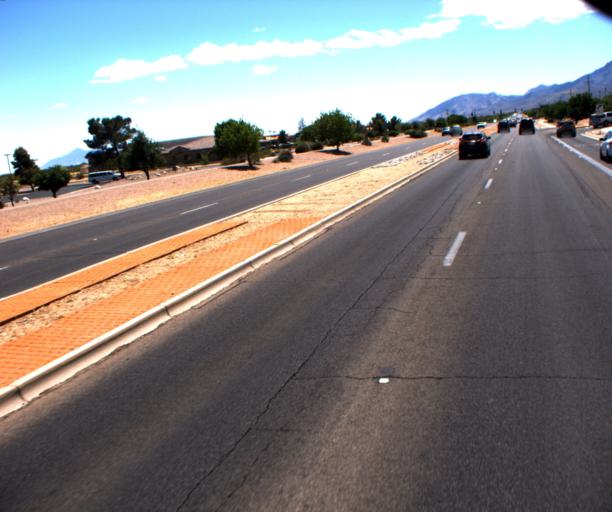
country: US
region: Arizona
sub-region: Cochise County
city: Sierra Vista
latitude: 31.5317
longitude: -110.2574
